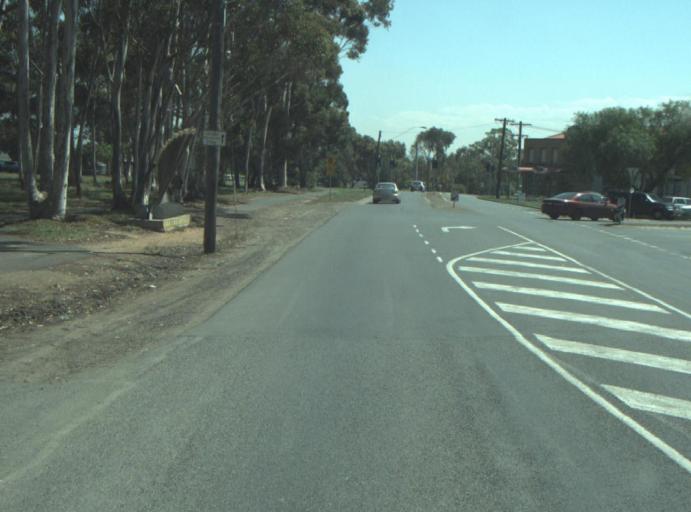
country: AU
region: Victoria
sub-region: Greater Geelong
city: Lara
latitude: -38.0236
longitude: 144.4095
